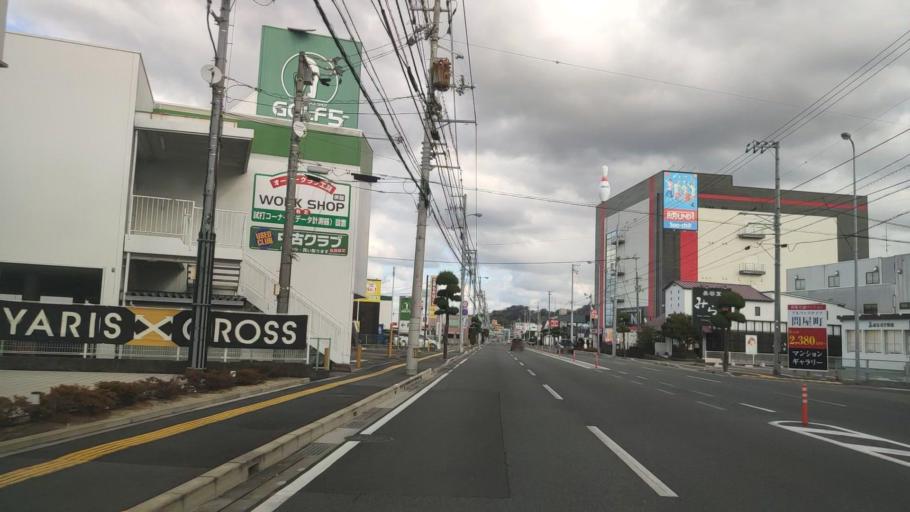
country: JP
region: Ehime
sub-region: Shikoku-chuo Shi
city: Matsuyama
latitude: 33.8652
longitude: 132.7507
